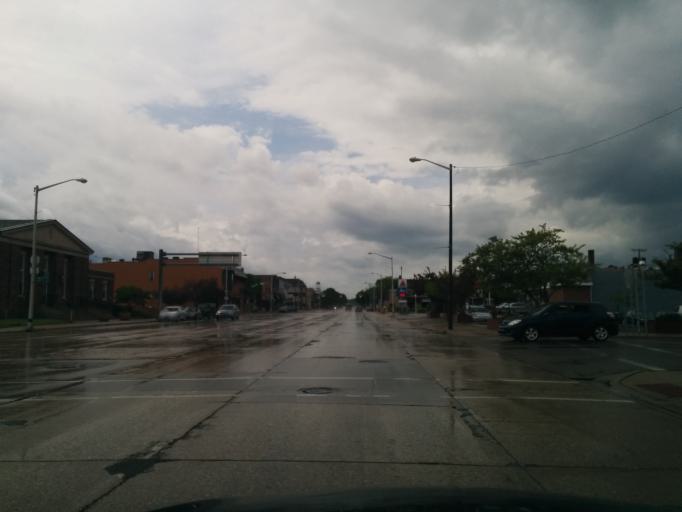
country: US
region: Michigan
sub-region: Berrien County
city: Saint Joseph
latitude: 42.1101
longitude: -86.4799
